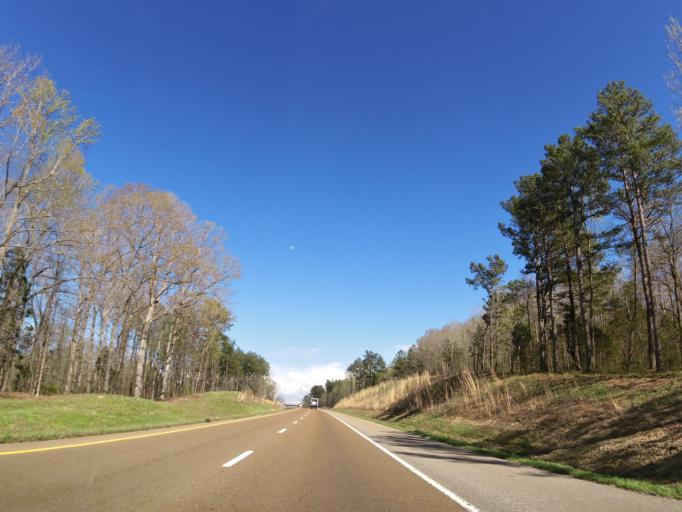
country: US
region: Tennessee
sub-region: Decatur County
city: Parsons
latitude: 35.8143
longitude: -88.2139
